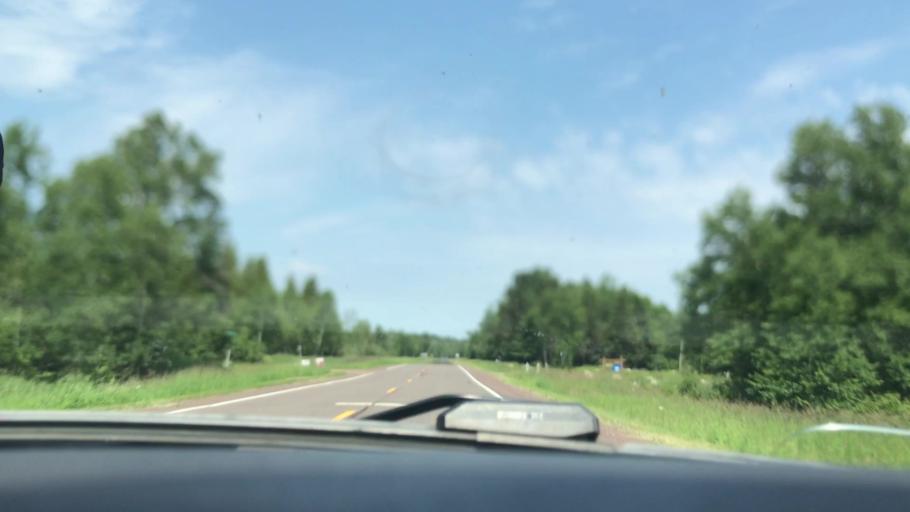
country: US
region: Minnesota
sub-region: Lake County
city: Silver Bay
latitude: 47.4879
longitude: -90.9869
